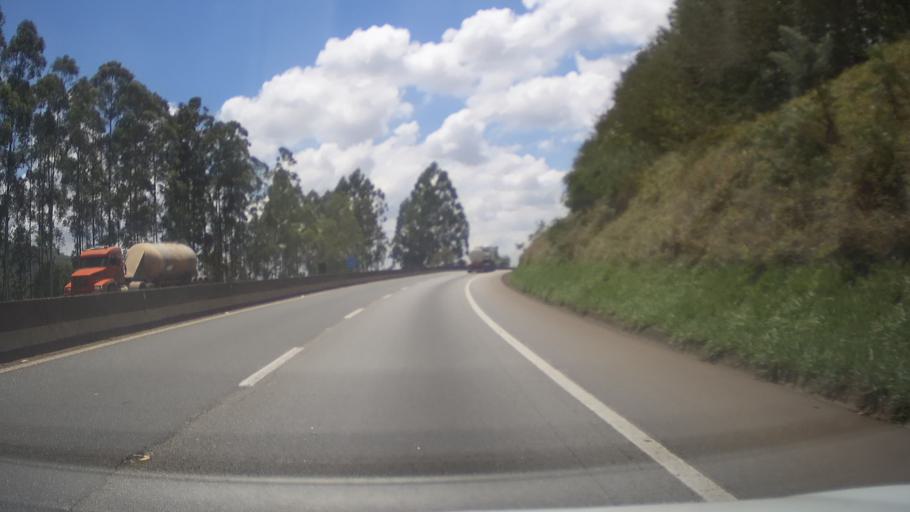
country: BR
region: Minas Gerais
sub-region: Campanha
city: Campanha
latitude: -21.8067
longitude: -45.4789
